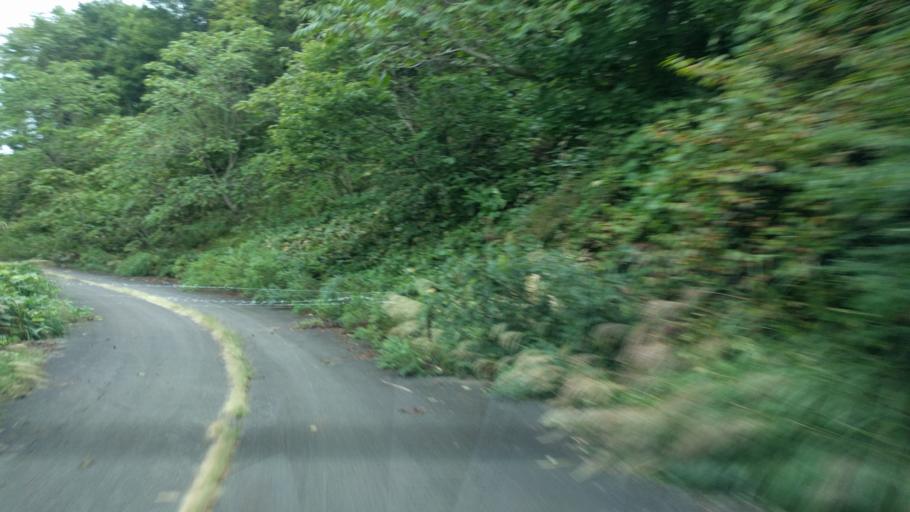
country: JP
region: Fukushima
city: Kitakata
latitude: 37.4601
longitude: 139.7789
